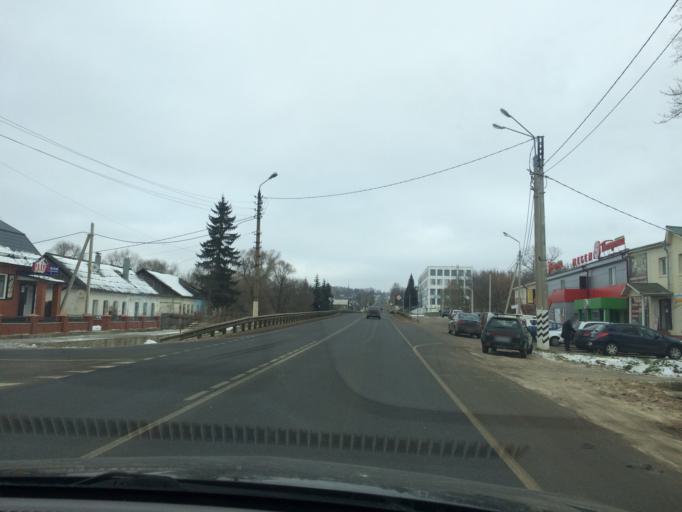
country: RU
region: Tula
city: Plavsk
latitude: 53.7103
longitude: 37.2953
